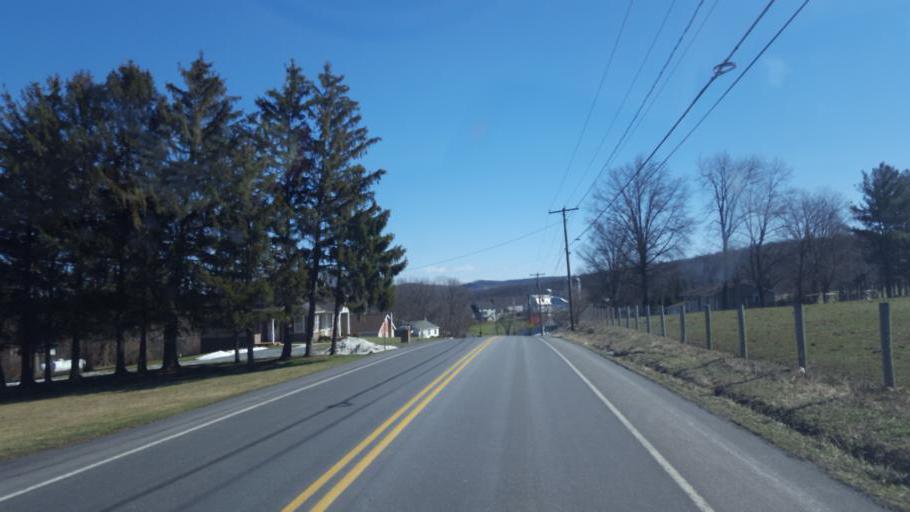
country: US
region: Pennsylvania
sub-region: Lancaster County
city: Terre Hill
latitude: 40.1588
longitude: -76.0184
